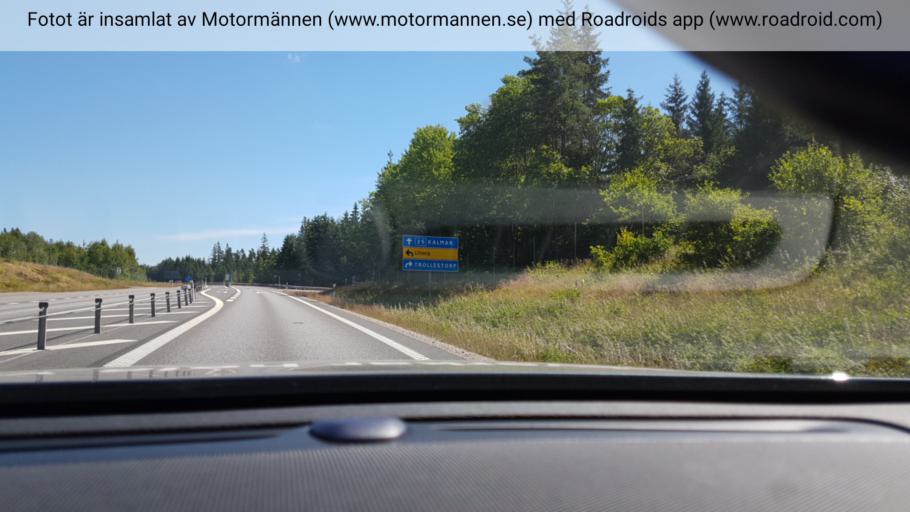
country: SE
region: Kronoberg
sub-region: Ljungby Kommun
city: Ljungby
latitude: 56.7621
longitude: 13.7856
